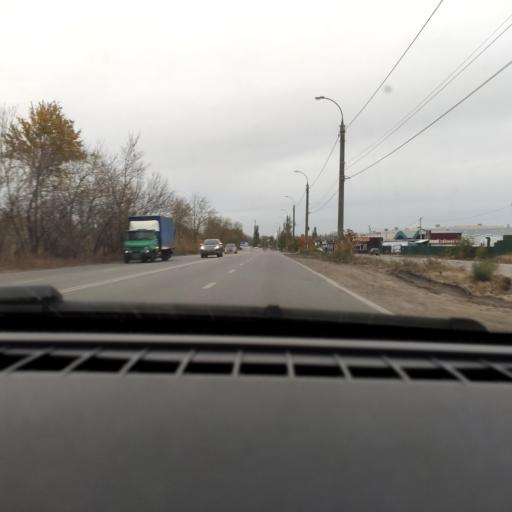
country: RU
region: Voronezj
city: Maslovka
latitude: 51.6108
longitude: 39.2568
